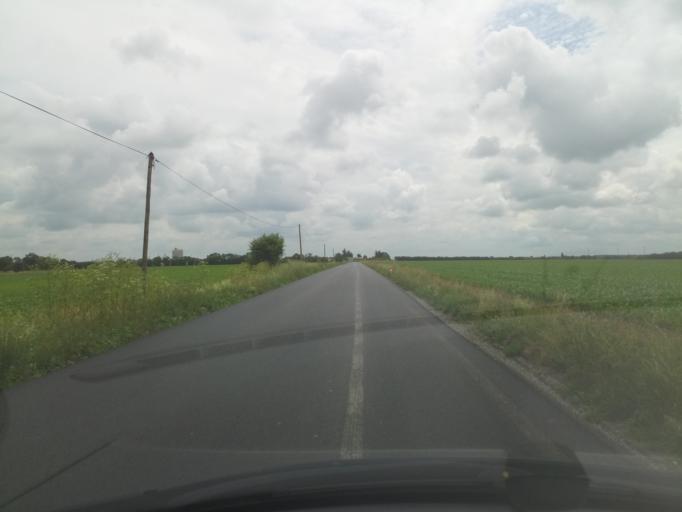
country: FR
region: Poitou-Charentes
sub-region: Departement de la Charente-Maritime
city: Saint-Jean-de-Liversay
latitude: 46.2703
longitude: -0.8934
